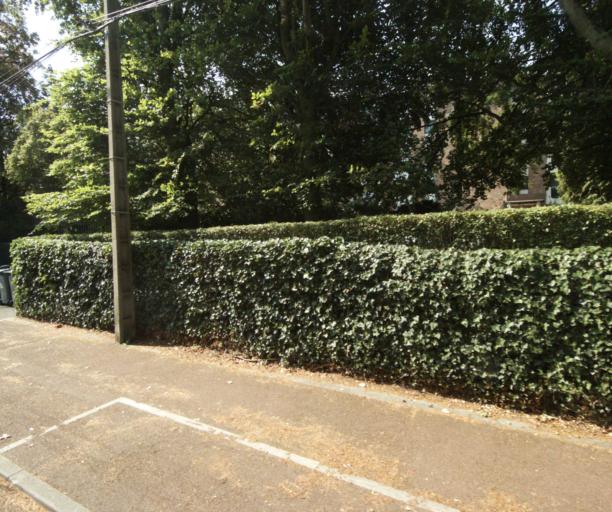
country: FR
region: Nord-Pas-de-Calais
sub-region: Departement du Nord
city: Mouvaux
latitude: 50.7079
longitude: 3.1389
